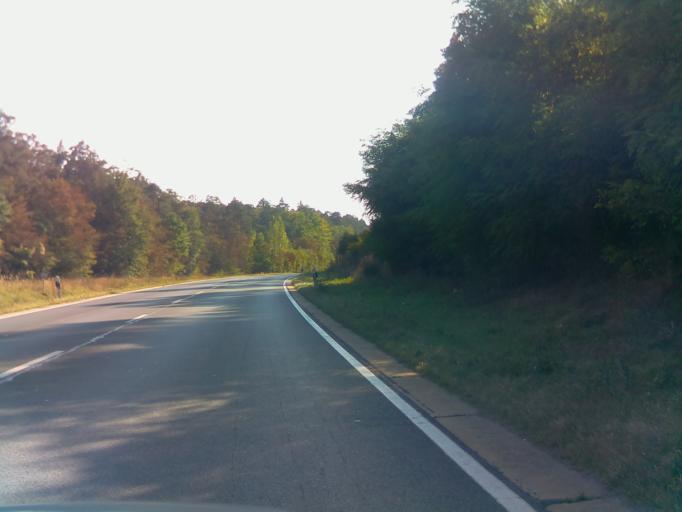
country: DE
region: Bavaria
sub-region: Regierungsbezirk Unterfranken
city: Albertshofen
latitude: 49.7766
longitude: 10.2044
